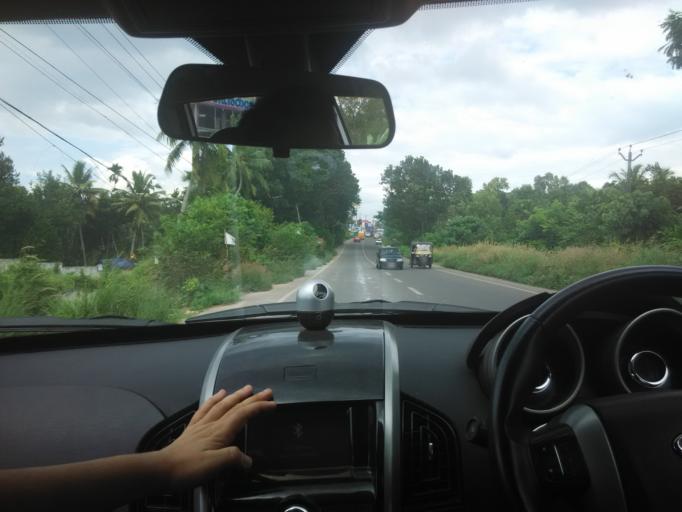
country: IN
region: Kerala
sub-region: Thiruvananthapuram
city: Attingal
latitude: 8.6398
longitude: 76.8446
